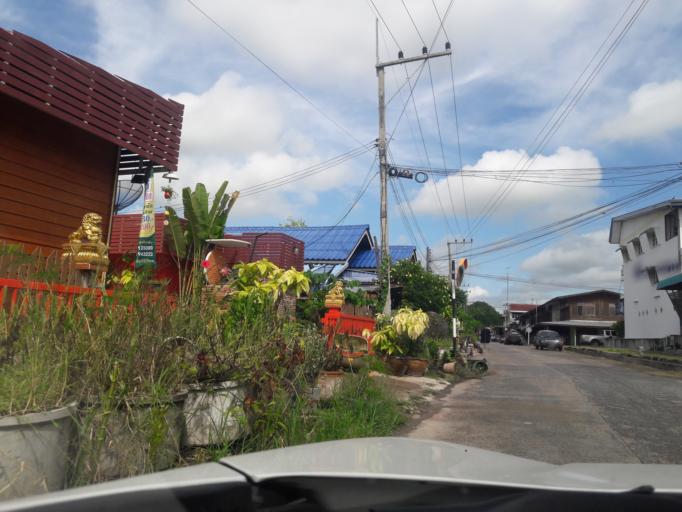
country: TH
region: Nakhon Sawan
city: Tak Fa
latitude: 15.3448
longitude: 100.4945
